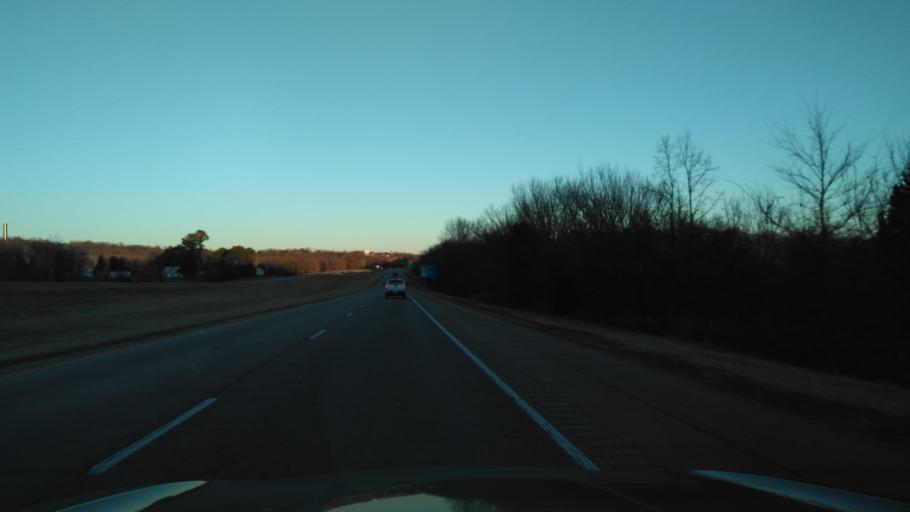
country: US
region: Arkansas
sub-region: Crawford County
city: Van Buren
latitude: 35.4624
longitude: -94.4171
